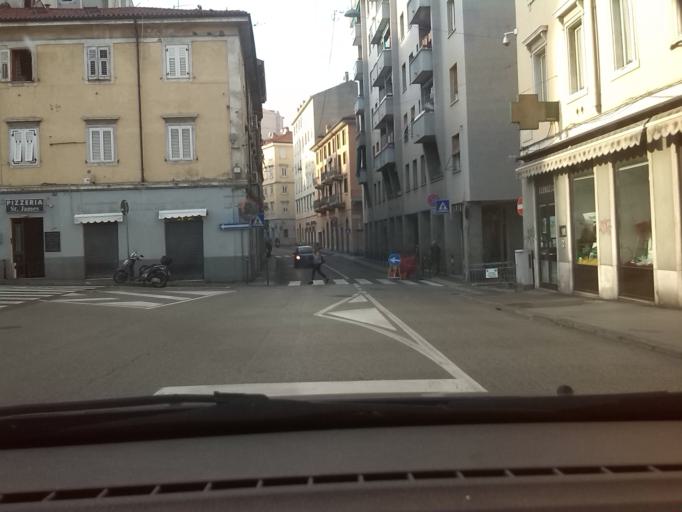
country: IT
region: Friuli Venezia Giulia
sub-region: Provincia di Trieste
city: Trieste
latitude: 45.6433
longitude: 13.7797
